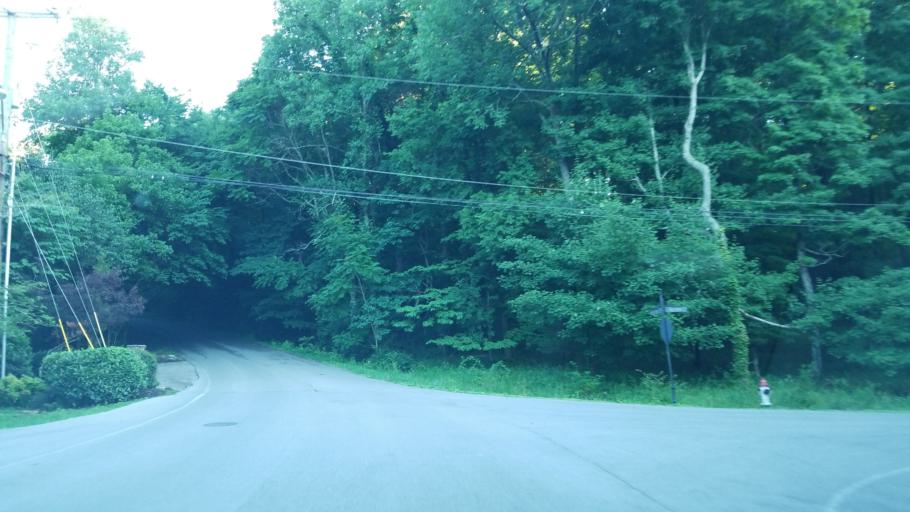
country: US
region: Tennessee
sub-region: Williamson County
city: Brentwood
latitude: 36.0433
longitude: -86.7918
